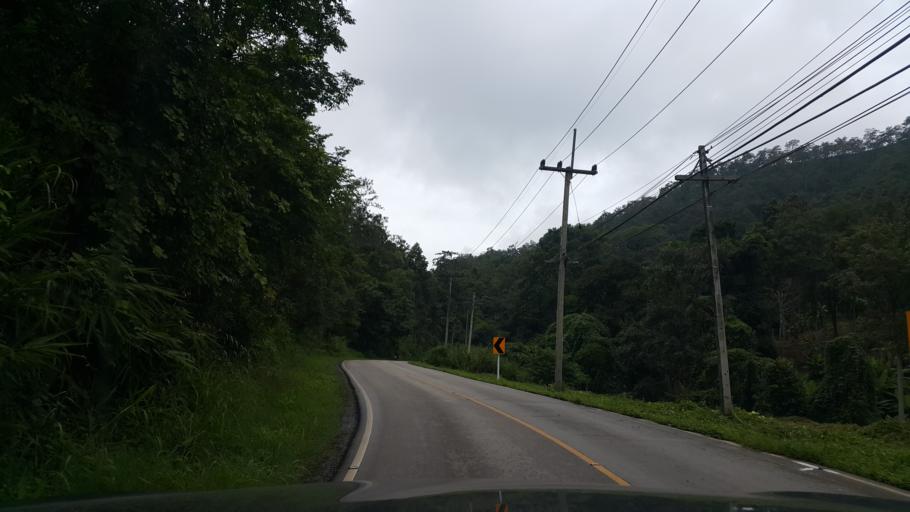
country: TH
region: Chiang Mai
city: Samoeng
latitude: 18.8682
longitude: 98.7193
